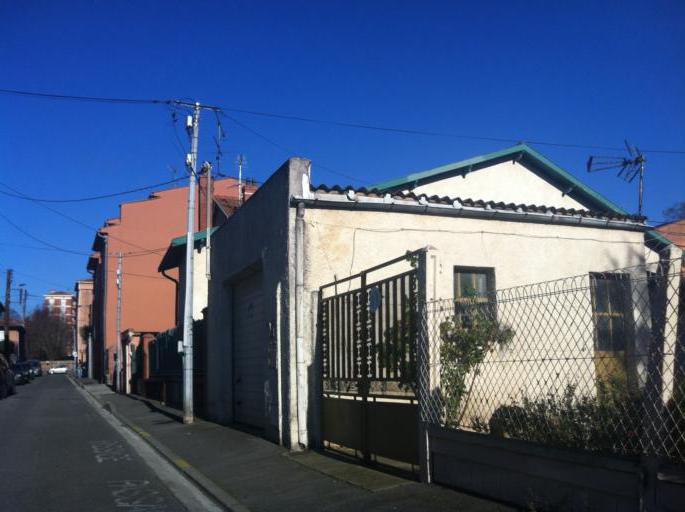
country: FR
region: Midi-Pyrenees
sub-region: Departement de la Haute-Garonne
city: Toulouse
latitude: 43.5835
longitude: 1.4680
